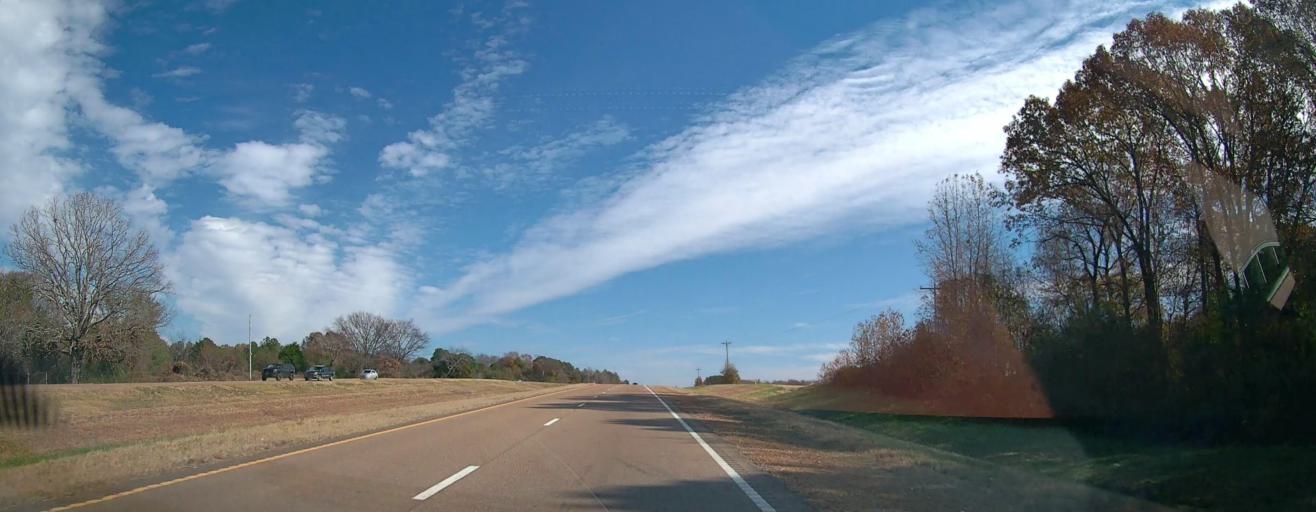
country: US
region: Mississippi
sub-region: Benton County
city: Ashland
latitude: 34.9459
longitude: -89.3270
